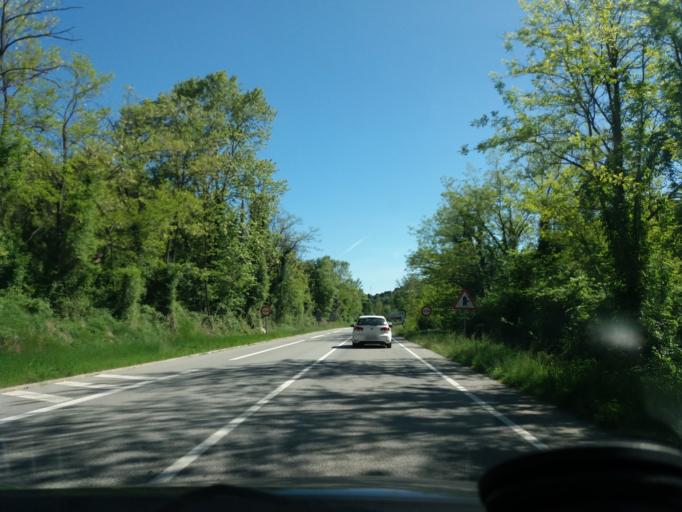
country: ES
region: Catalonia
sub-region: Provincia de Barcelona
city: Gironella
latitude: 42.0548
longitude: 1.8737
